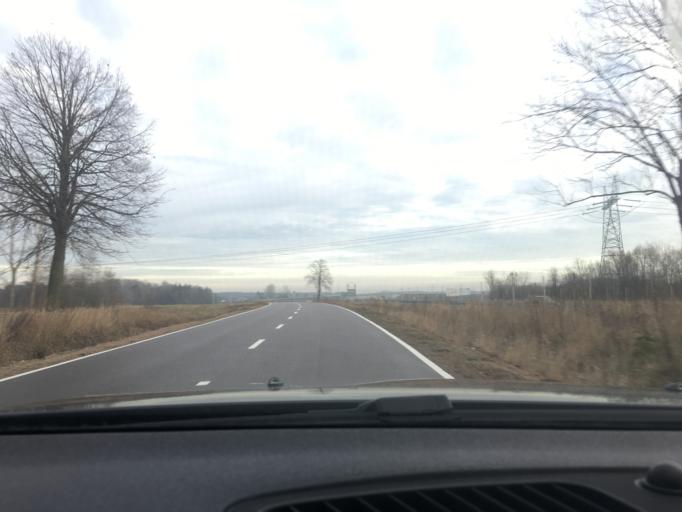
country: PL
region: Swietokrzyskie
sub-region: Powiat jedrzejowski
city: Jedrzejow
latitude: 50.6546
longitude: 20.3236
